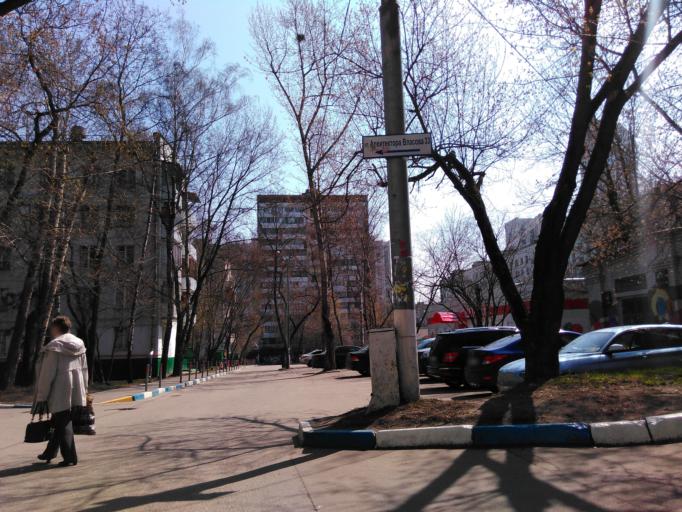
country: RU
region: Moskovskaya
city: Semenovskoye
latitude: 55.6688
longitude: 37.5445
